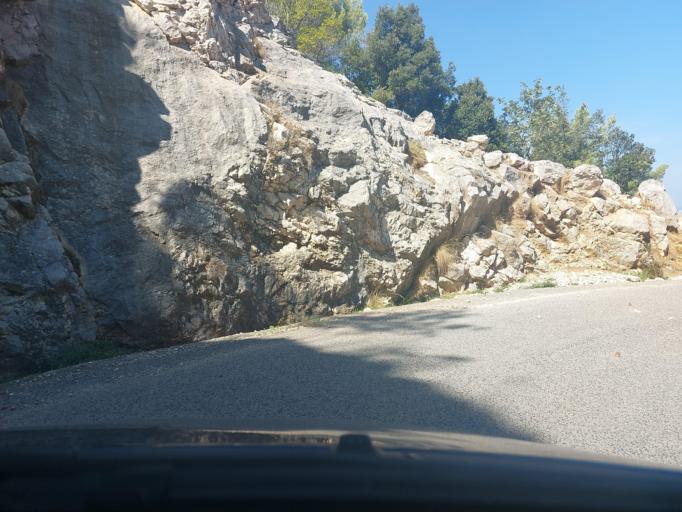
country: HR
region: Dubrovacko-Neretvanska
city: Smokvica
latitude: 42.7435
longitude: 16.8453
